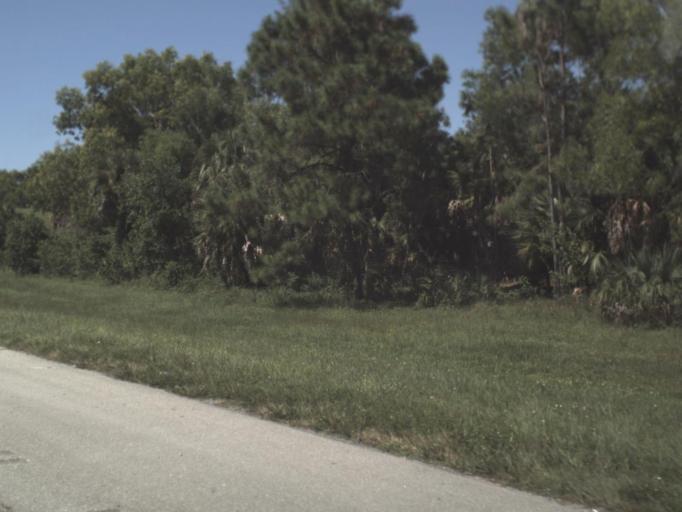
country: US
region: Florida
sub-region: Collier County
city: Golden Gate
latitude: 26.1644
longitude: -81.7172
